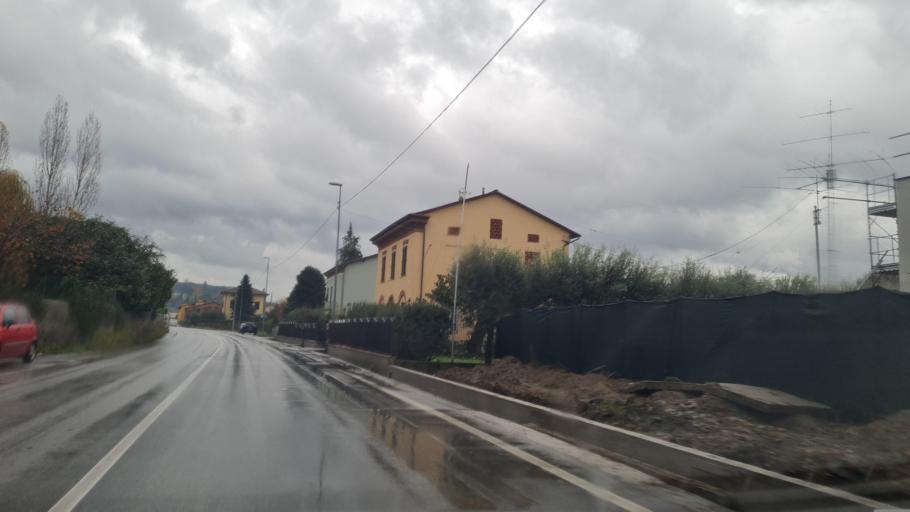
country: IT
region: Tuscany
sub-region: Provincia di Lucca
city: Lucca
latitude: 43.8602
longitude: 10.4913
